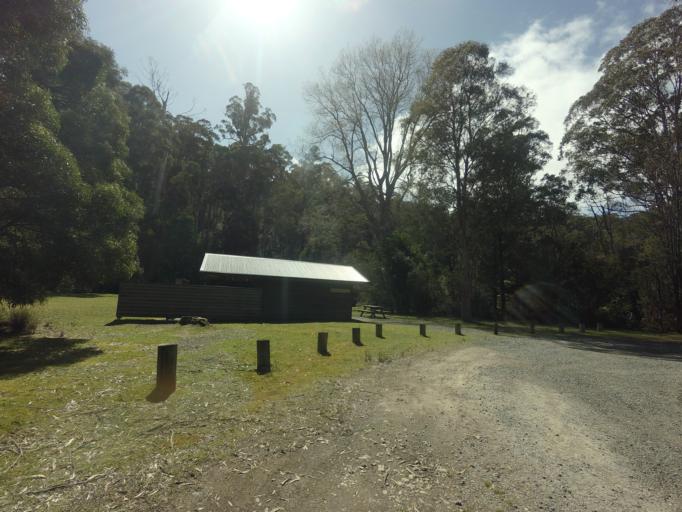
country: AU
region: Tasmania
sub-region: Derwent Valley
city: New Norfolk
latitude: -42.6814
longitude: 146.7191
